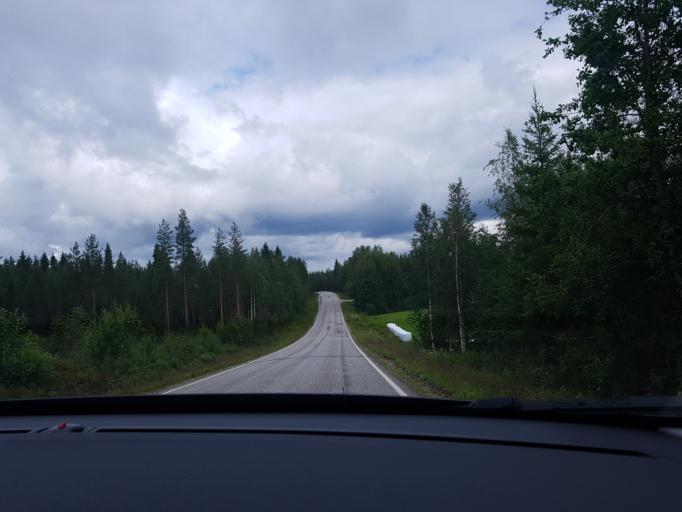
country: FI
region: Kainuu
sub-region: Kehys-Kainuu
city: Kuhmo
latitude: 64.2277
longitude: 29.4496
